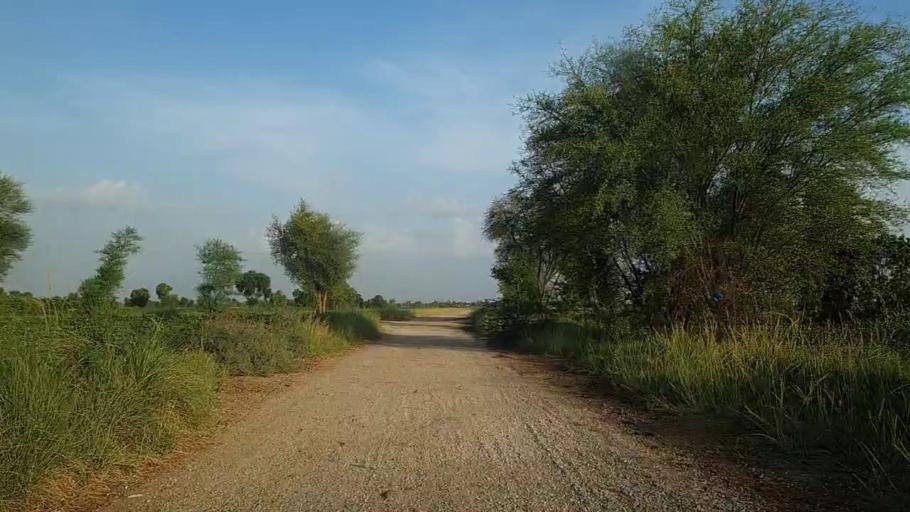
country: PK
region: Sindh
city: Karaundi
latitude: 27.0543
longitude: 68.4028
